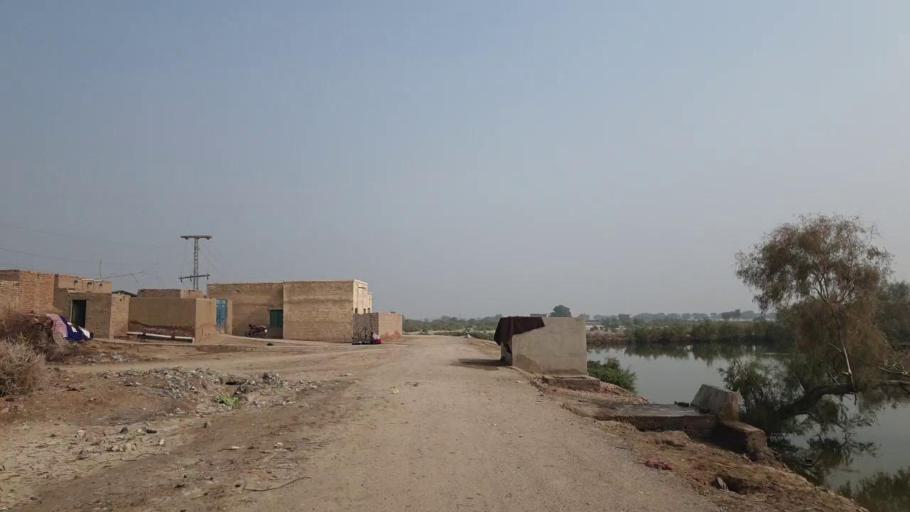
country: PK
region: Sindh
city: Bhan
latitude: 26.5072
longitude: 67.6747
